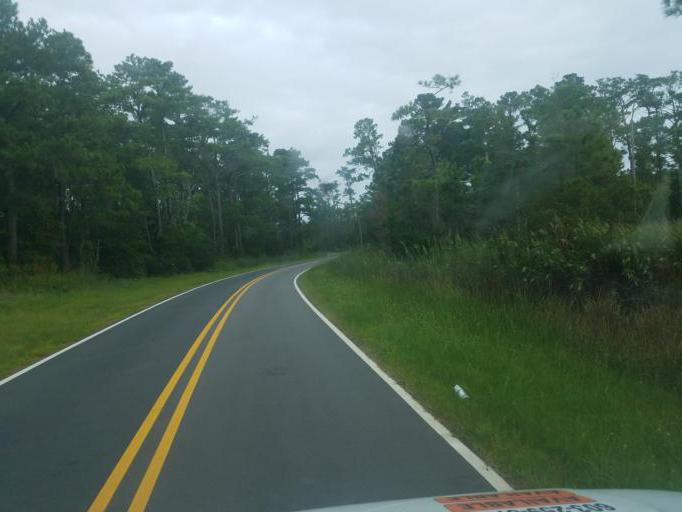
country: US
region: North Carolina
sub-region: Dare County
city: Manteo
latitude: 35.8785
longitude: -75.7589
